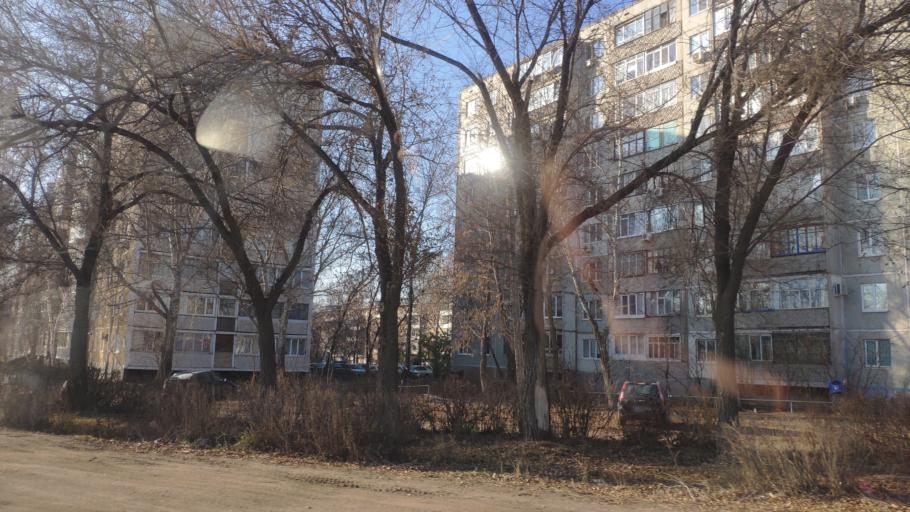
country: RU
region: Orenburg
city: Prigorodnyy
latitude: 51.7785
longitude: 55.1902
